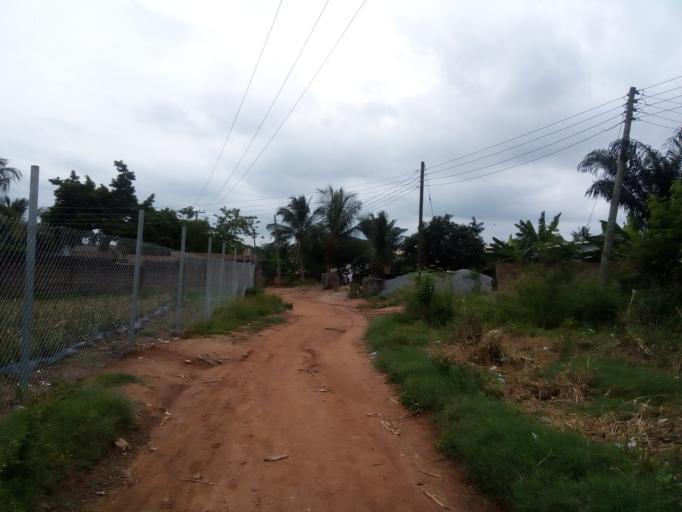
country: GH
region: Eastern
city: Nsawam
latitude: 5.7807
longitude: -0.3385
